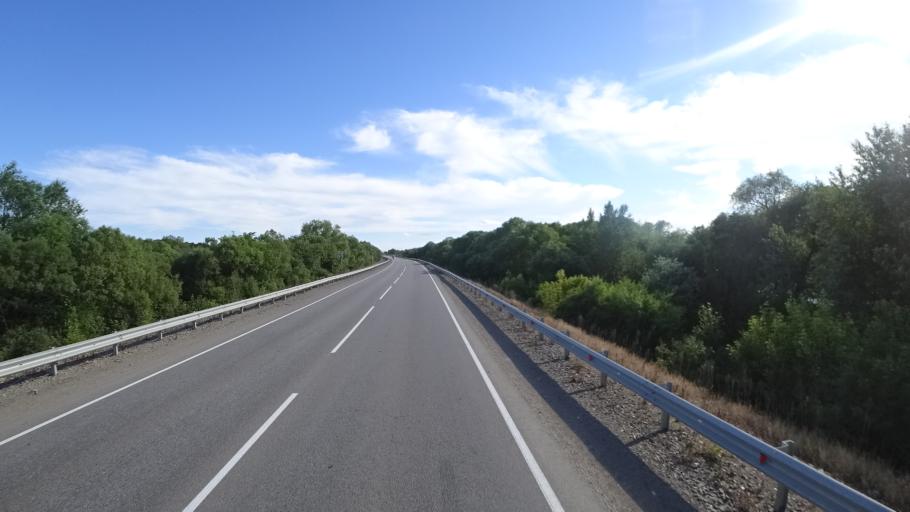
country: RU
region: Khabarovsk Krai
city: Khor
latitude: 47.8825
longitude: 134.9717
